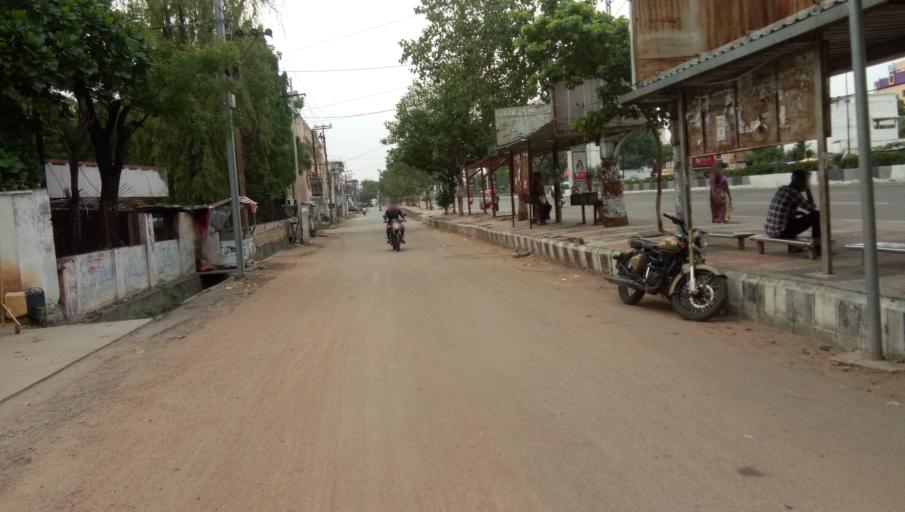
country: IN
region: Telangana
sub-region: Rangareddi
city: Lal Bahadur Nagar
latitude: 17.3556
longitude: 78.5453
